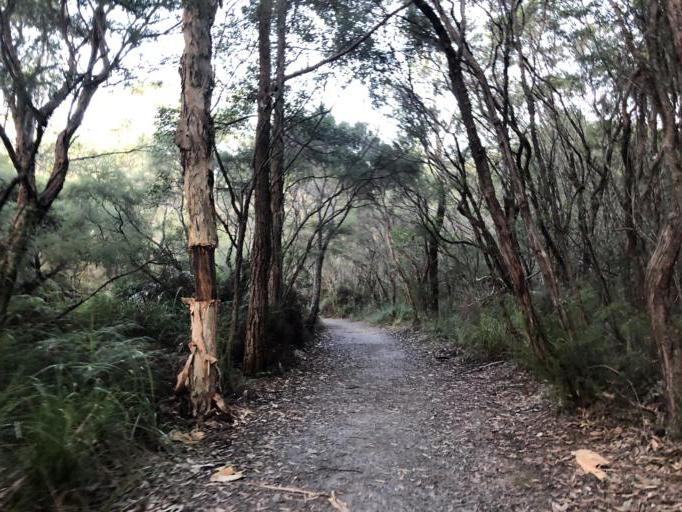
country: AU
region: New South Wales
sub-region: Coffs Harbour
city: Coffs Harbour
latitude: -30.3011
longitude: 153.1315
